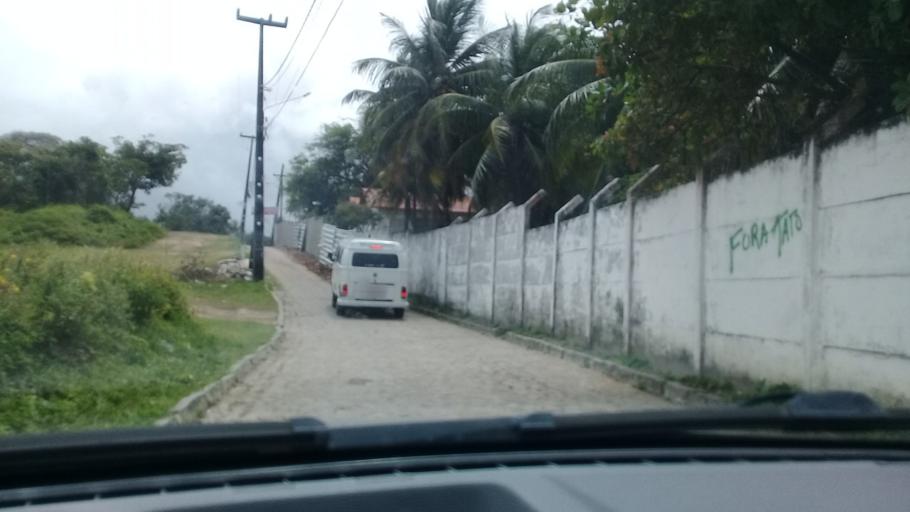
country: BR
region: Pernambuco
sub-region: Itamaraca
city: Itamaraca
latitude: -7.7279
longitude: -34.8270
